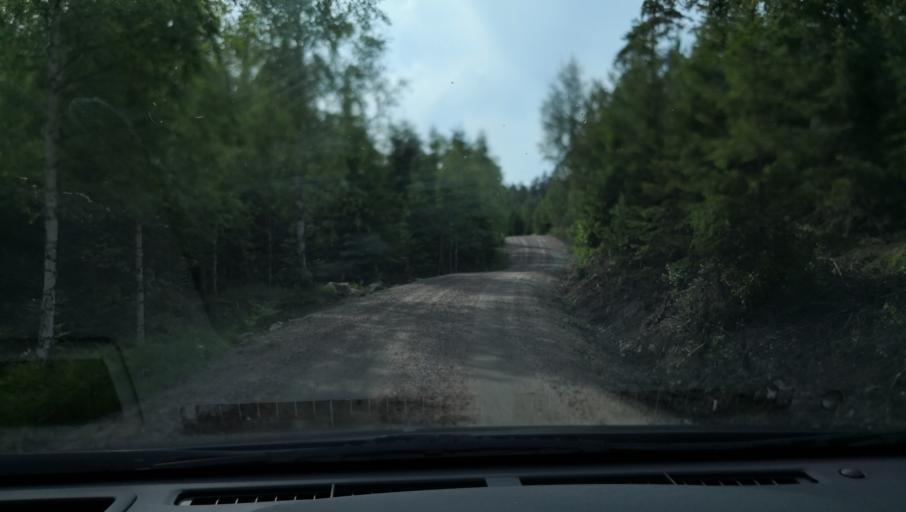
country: SE
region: Vaestmanland
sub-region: Arboga Kommun
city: Tyringe
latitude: 59.3433
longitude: 15.9191
